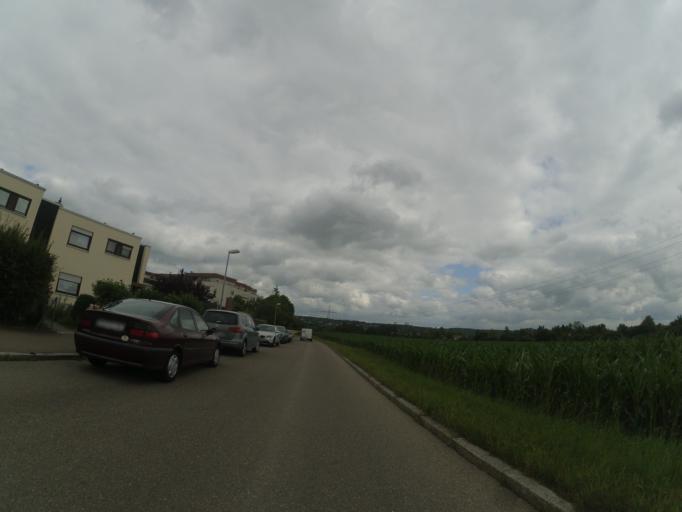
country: DE
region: Bavaria
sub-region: Swabia
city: Neu-Ulm
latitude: 48.4046
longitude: 10.0264
